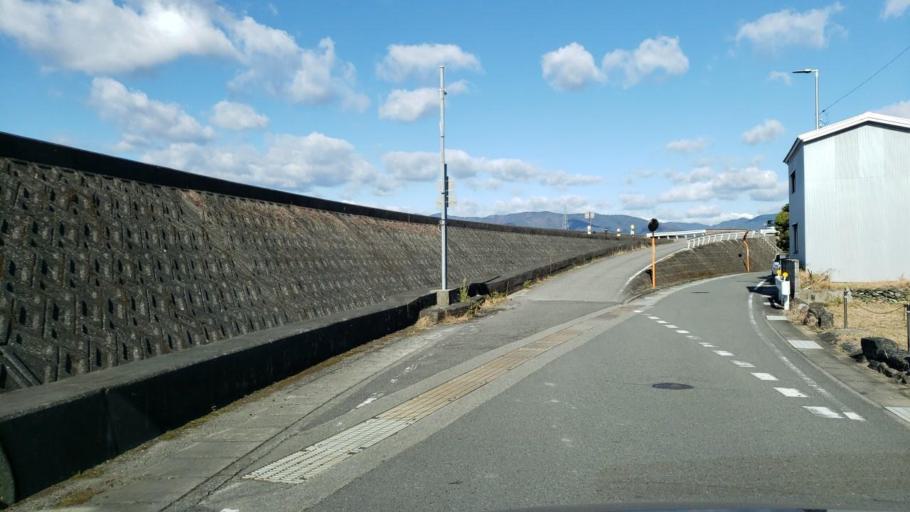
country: JP
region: Tokushima
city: Kamojimacho-jogejima
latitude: 34.0661
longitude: 134.3172
